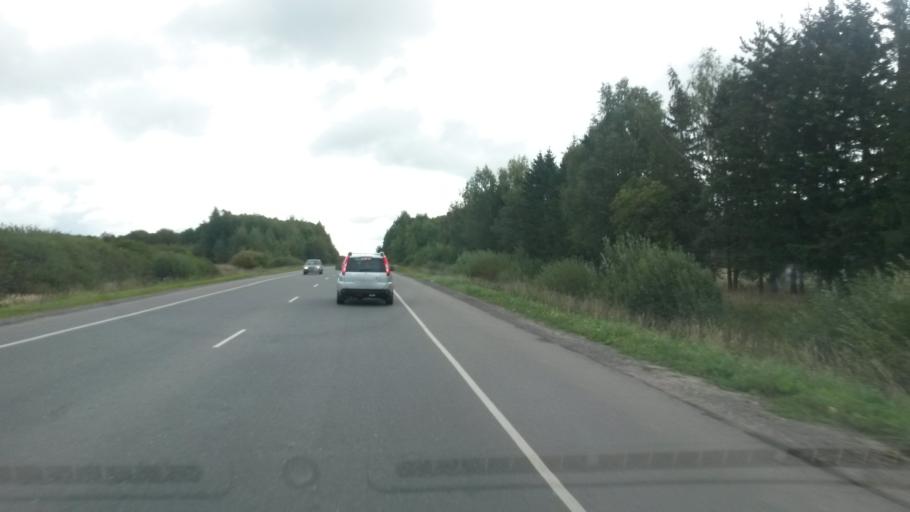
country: RU
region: Ivanovo
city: Rodniki
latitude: 57.0882
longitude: 41.6636
